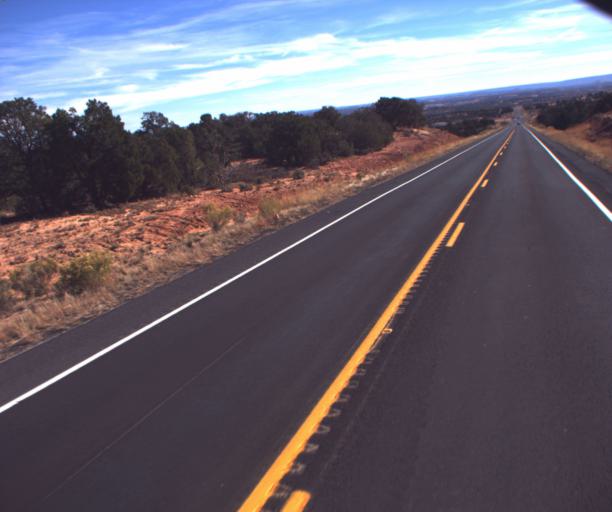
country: US
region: Arizona
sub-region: Coconino County
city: Kaibito
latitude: 36.5823
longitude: -110.8046
